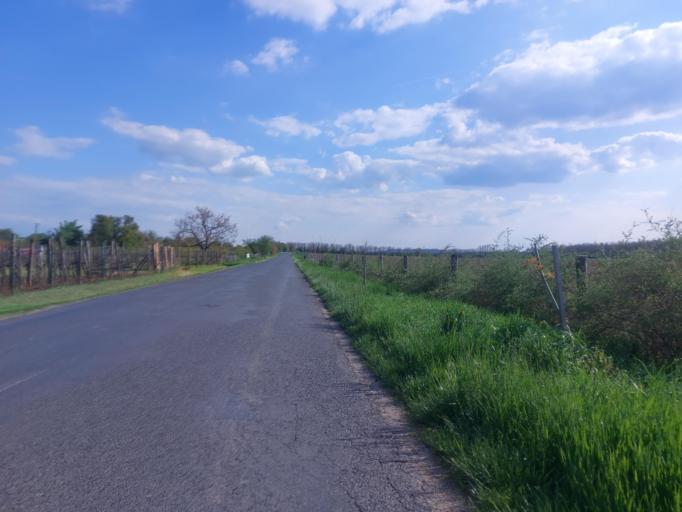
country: HU
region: Veszprem
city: Devecser
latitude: 47.1489
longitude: 17.3553
